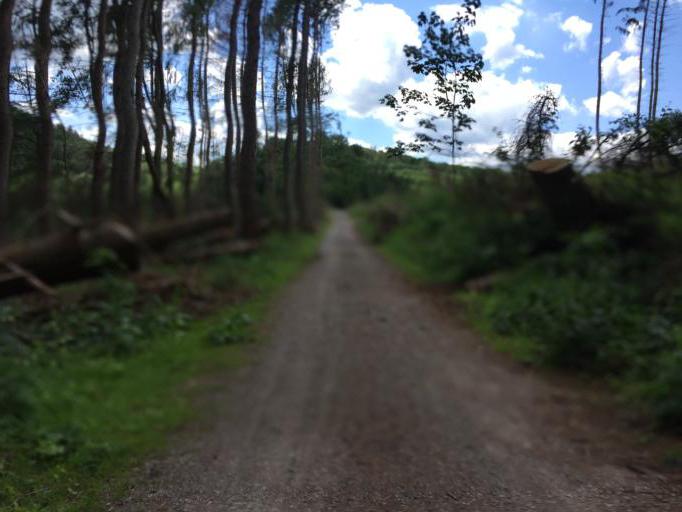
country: DE
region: Rheinland-Pfalz
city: Holler
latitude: 50.4249
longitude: 7.8578
